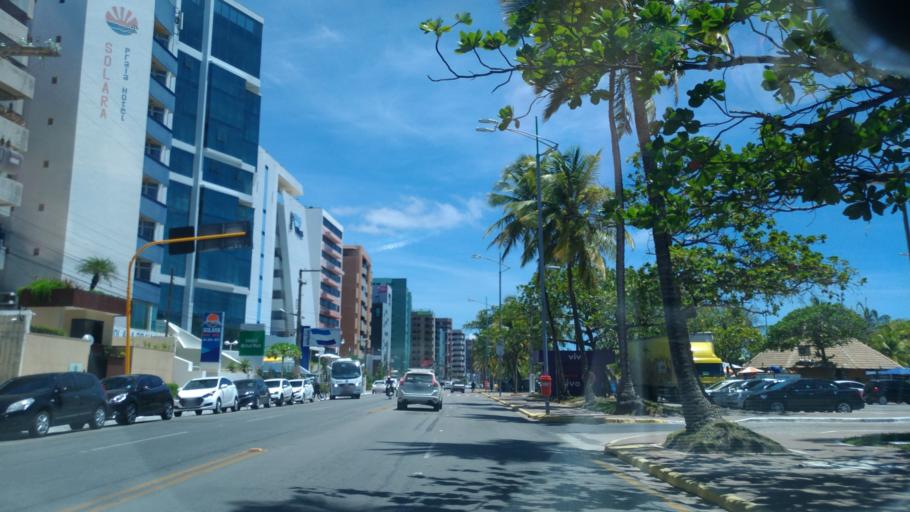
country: BR
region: Alagoas
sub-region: Maceio
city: Maceio
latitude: -9.6728
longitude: -35.7167
